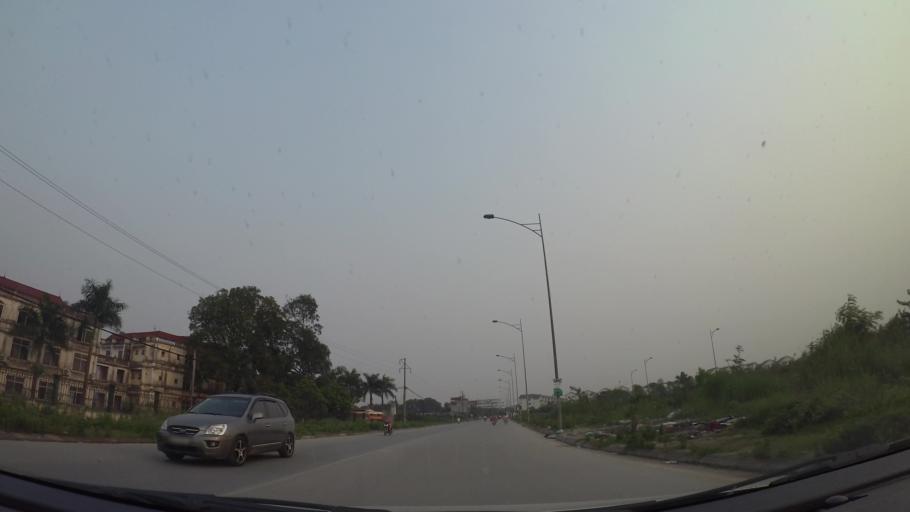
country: VN
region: Ha Noi
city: Cau Dien
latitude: 21.0016
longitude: 105.7239
